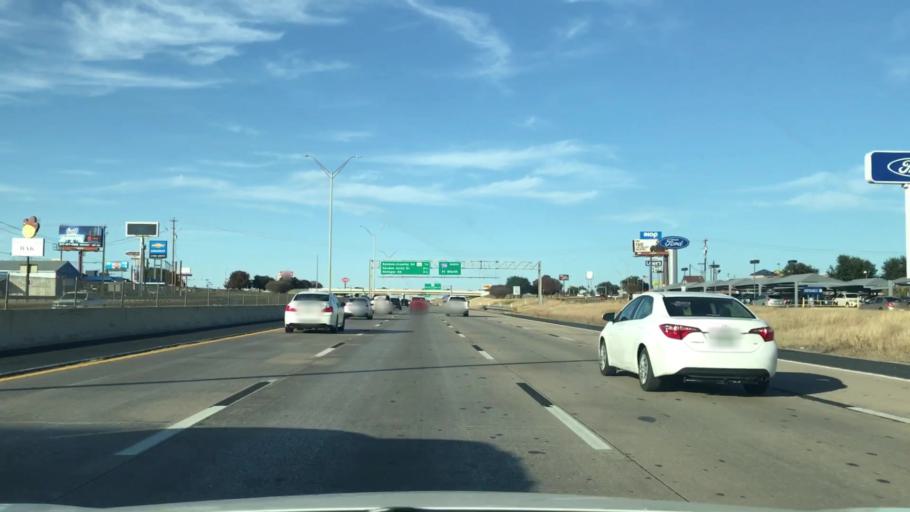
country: US
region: Texas
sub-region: Johnson County
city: Burleson
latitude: 32.5592
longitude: -97.3189
